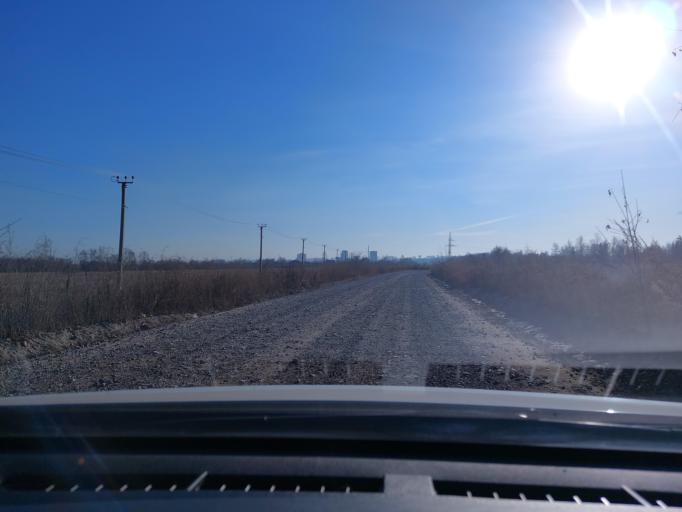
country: RU
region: Irkutsk
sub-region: Irkutskiy Rayon
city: Irkutsk
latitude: 52.3051
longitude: 104.2757
